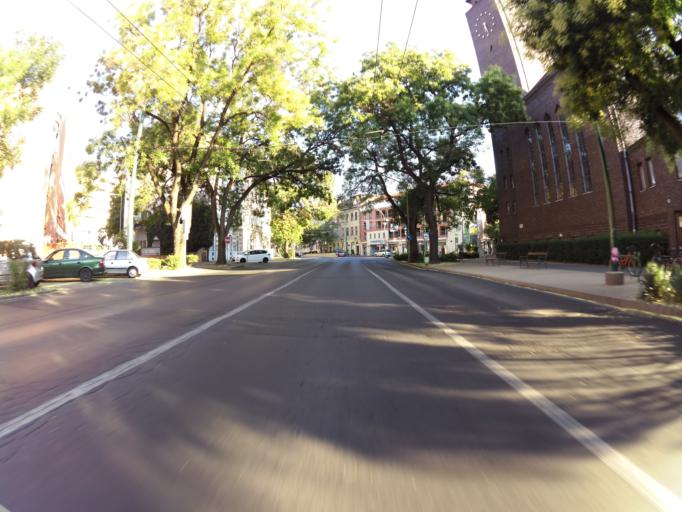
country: HU
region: Csongrad
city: Szeged
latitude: 46.2492
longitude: 20.1449
